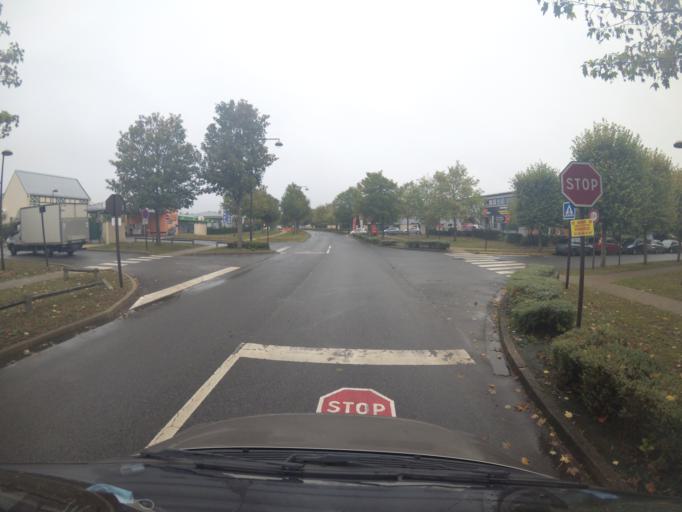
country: FR
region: Ile-de-France
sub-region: Departement de Seine-et-Marne
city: Ferrieres-en-Brie
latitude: 48.8276
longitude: 2.7029
